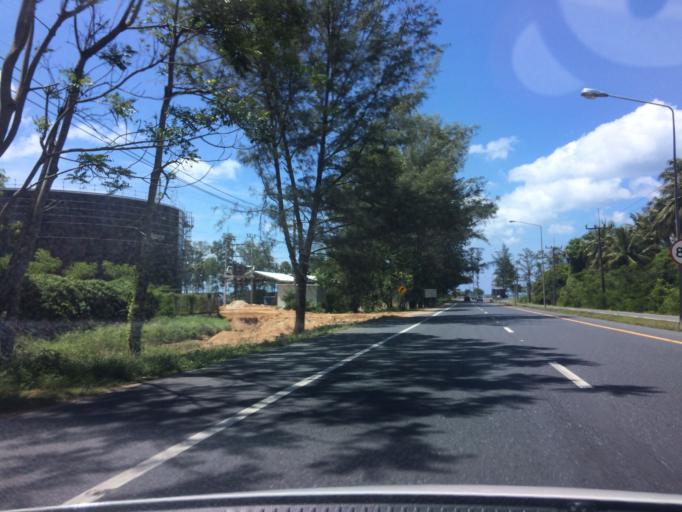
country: TH
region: Phuket
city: Thalang
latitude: 8.1833
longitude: 98.2924
